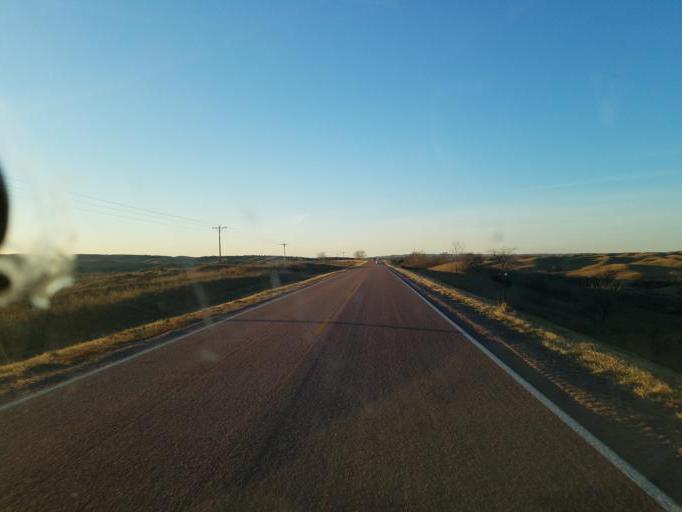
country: US
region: South Dakota
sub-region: Bon Homme County
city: Springfield
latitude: 42.7391
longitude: -97.9104
